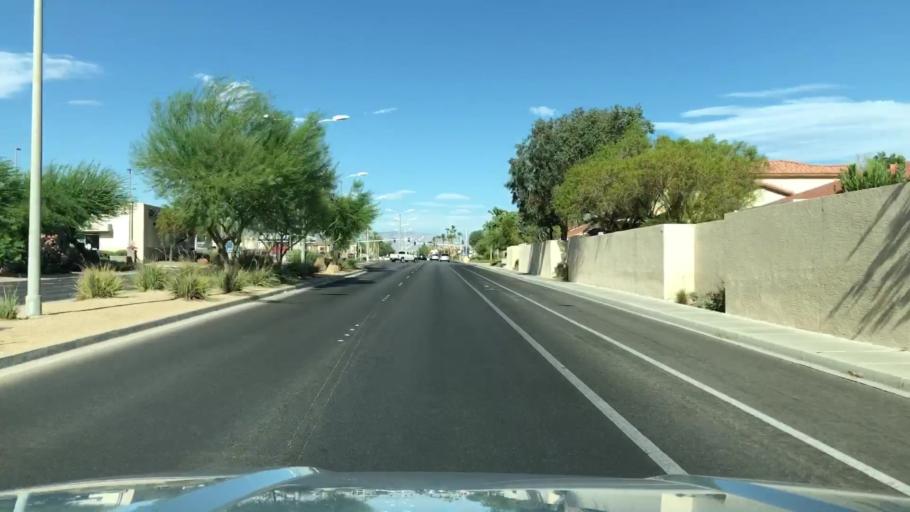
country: US
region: Nevada
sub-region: Clark County
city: Whitney
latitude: 36.0424
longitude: -115.0972
